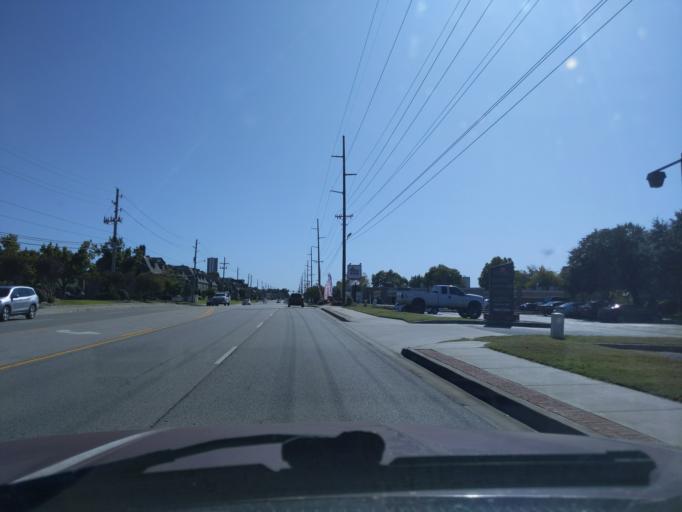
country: US
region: Oklahoma
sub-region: Tulsa County
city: Jenks
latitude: 36.0668
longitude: -95.9580
